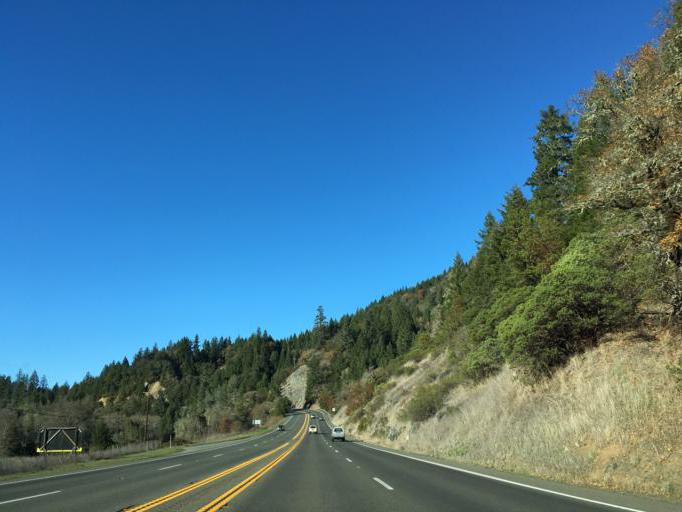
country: US
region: California
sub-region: Mendocino County
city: Brooktrails
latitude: 39.5185
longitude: -123.3916
